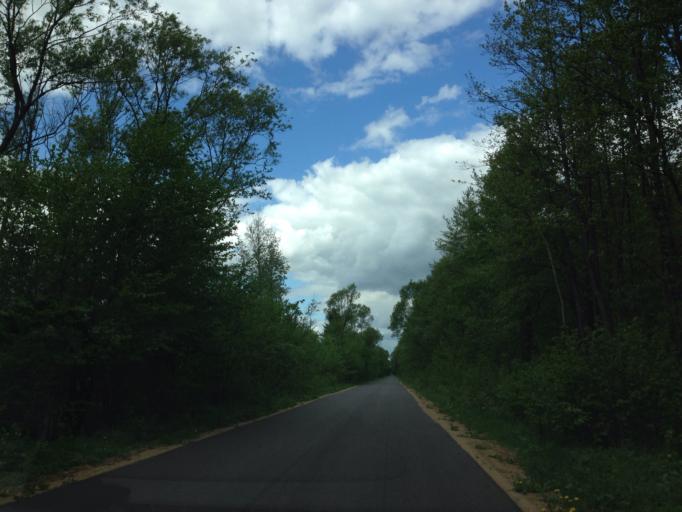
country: PL
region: Podlasie
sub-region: Powiat bialostocki
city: Tykocin
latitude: 53.3226
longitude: 22.6012
